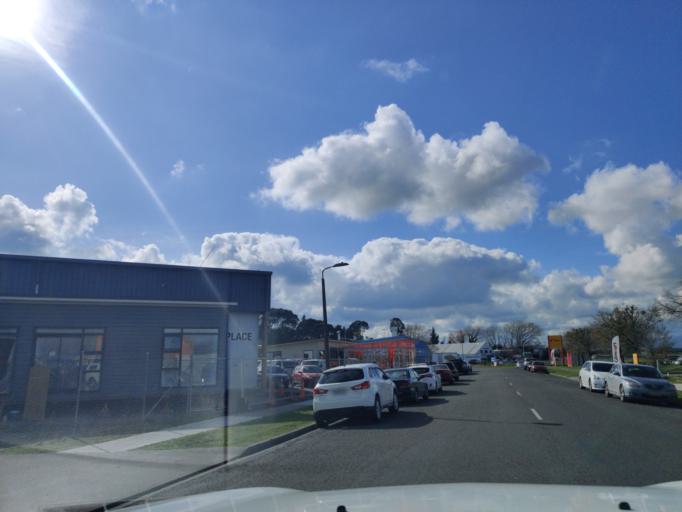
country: NZ
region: Manawatu-Wanganui
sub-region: Palmerston North City
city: Palmerston North
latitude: -40.3393
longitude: 175.6000
